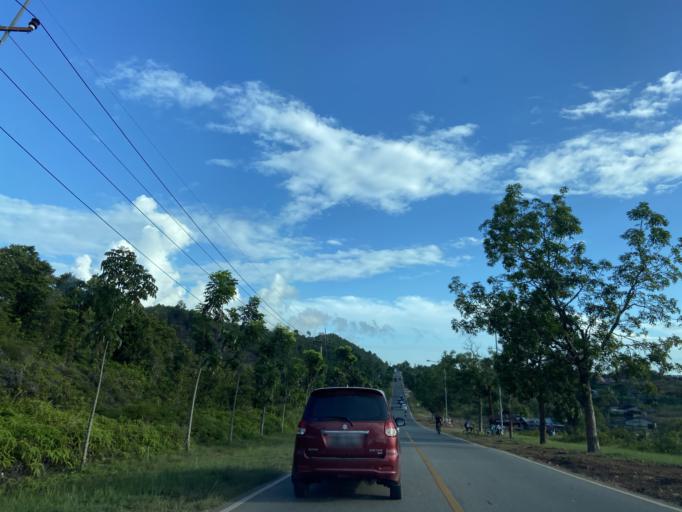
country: SG
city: Singapore
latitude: 0.9909
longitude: 104.0354
